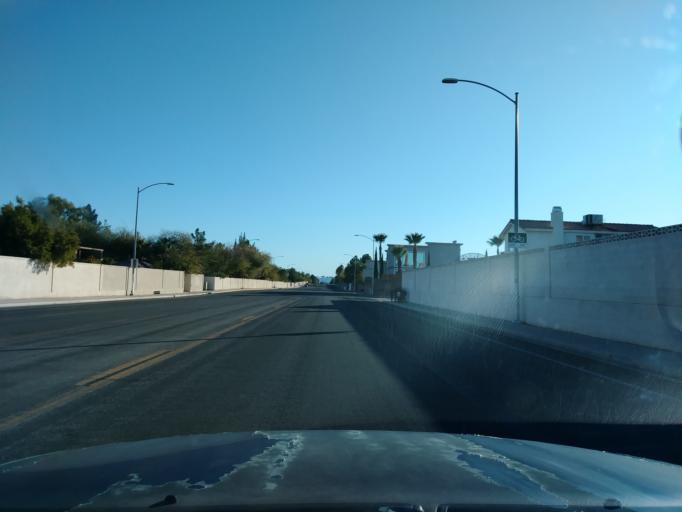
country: US
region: Nevada
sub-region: Clark County
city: Spring Valley
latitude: 36.1558
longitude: -115.2711
